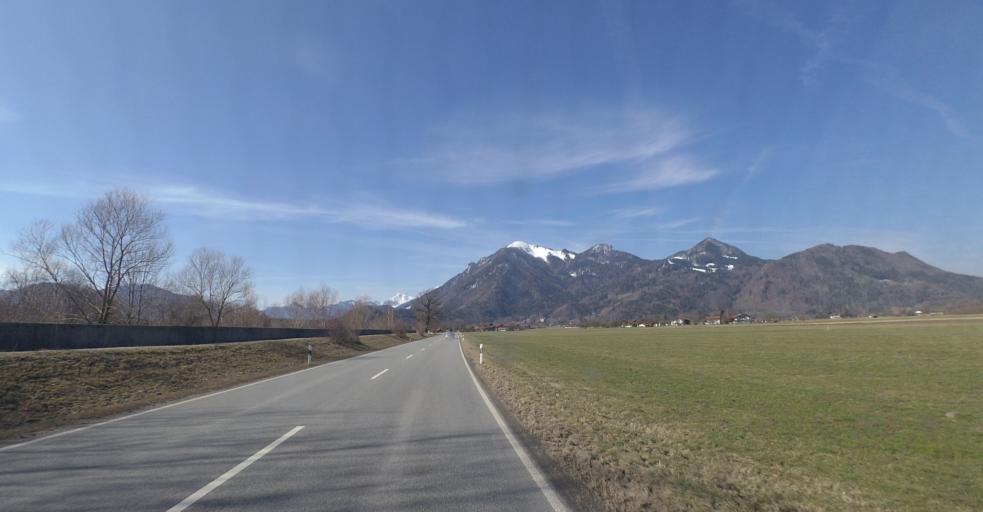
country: DE
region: Bavaria
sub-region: Upper Bavaria
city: Marquartstein
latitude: 47.7710
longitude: 12.4695
